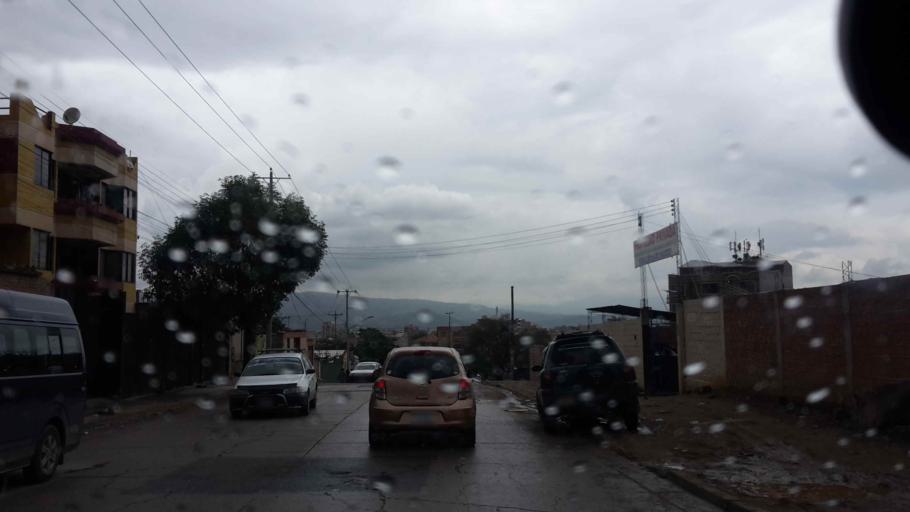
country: BO
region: Cochabamba
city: Cochabamba
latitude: -17.4211
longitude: -66.1521
